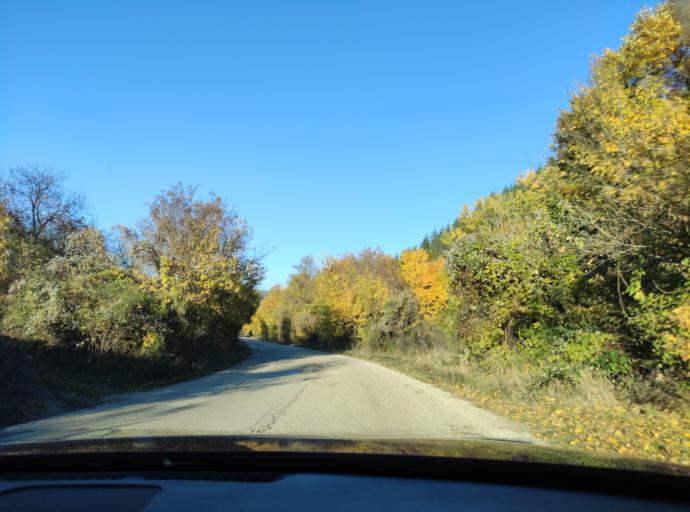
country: BG
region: Montana
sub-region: Obshtina Chiprovtsi
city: Chiprovtsi
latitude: 43.4165
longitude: 22.9502
